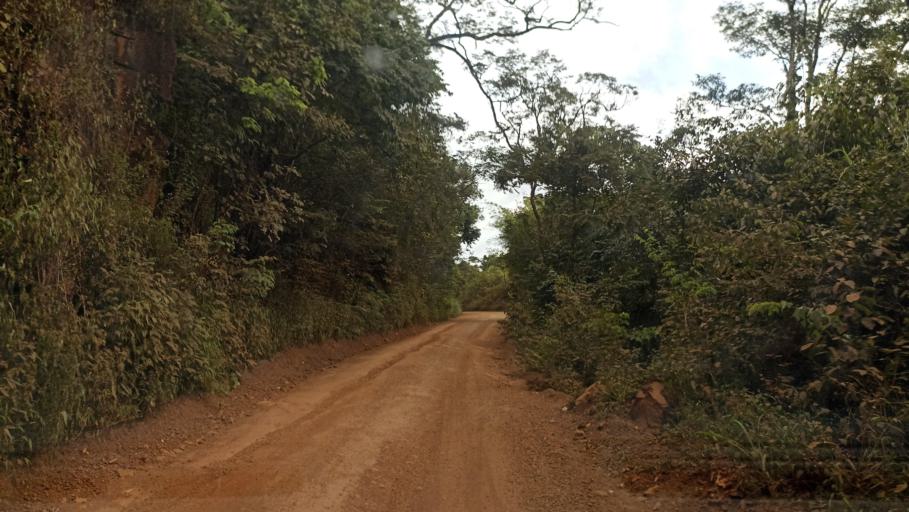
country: BR
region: Minas Gerais
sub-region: Itabirito
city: Itabirito
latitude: -20.3704
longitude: -43.7616
